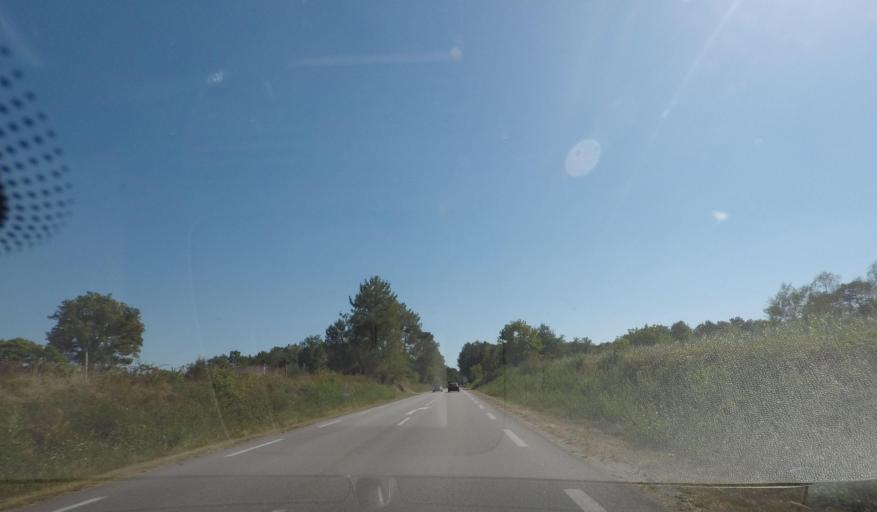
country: FR
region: Brittany
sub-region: Departement du Morbihan
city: Peaule
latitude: 47.5814
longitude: -2.3778
